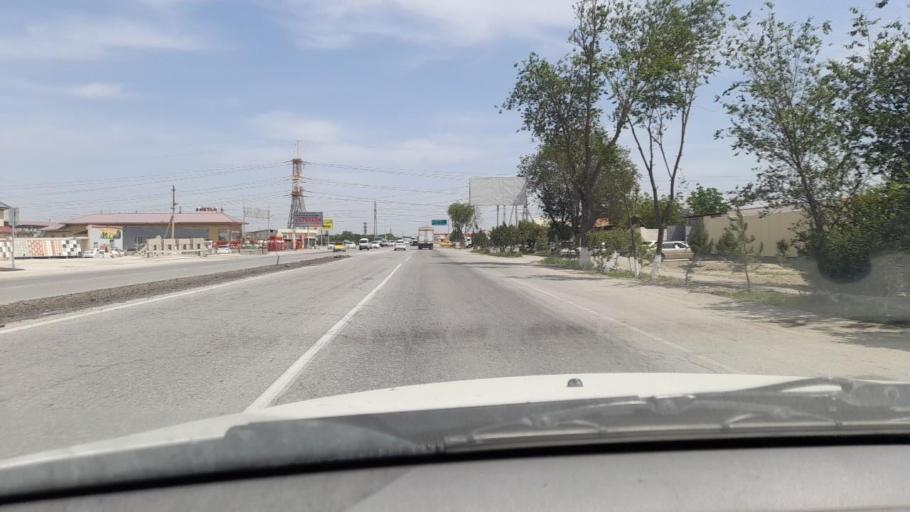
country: UZ
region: Navoiy
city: Beshrabot
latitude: 40.1469
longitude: 65.3111
